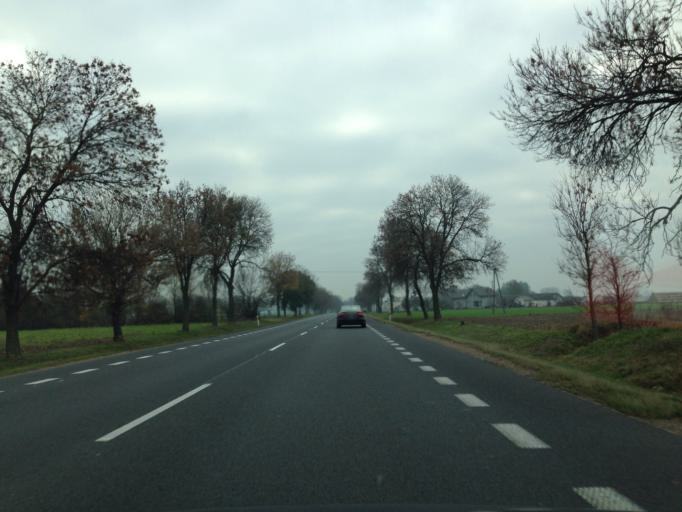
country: PL
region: Masovian Voivodeship
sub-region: Powiat plocki
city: Drobin
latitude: 52.7493
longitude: 19.9725
